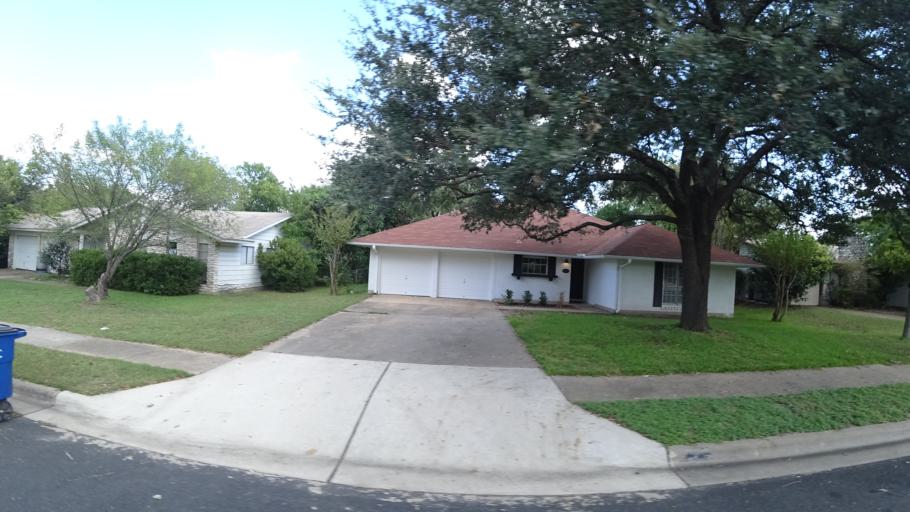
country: US
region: Texas
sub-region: Travis County
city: Wells Branch
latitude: 30.3620
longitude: -97.7142
